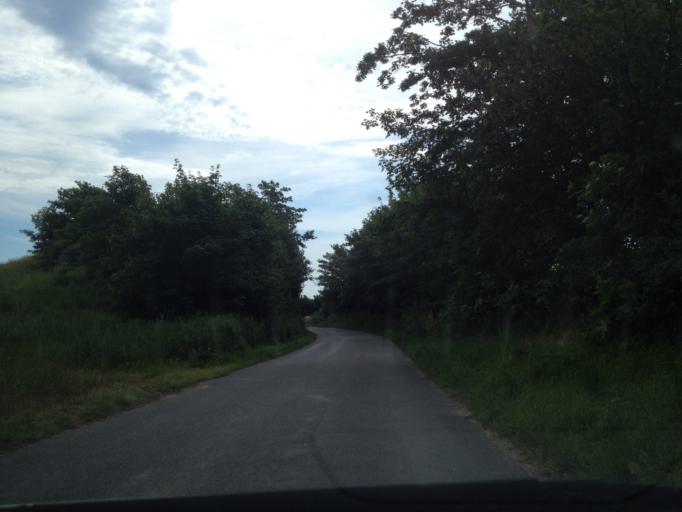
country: DK
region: Central Jutland
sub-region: Samso Kommune
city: Tranebjerg
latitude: 55.9671
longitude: 10.5437
